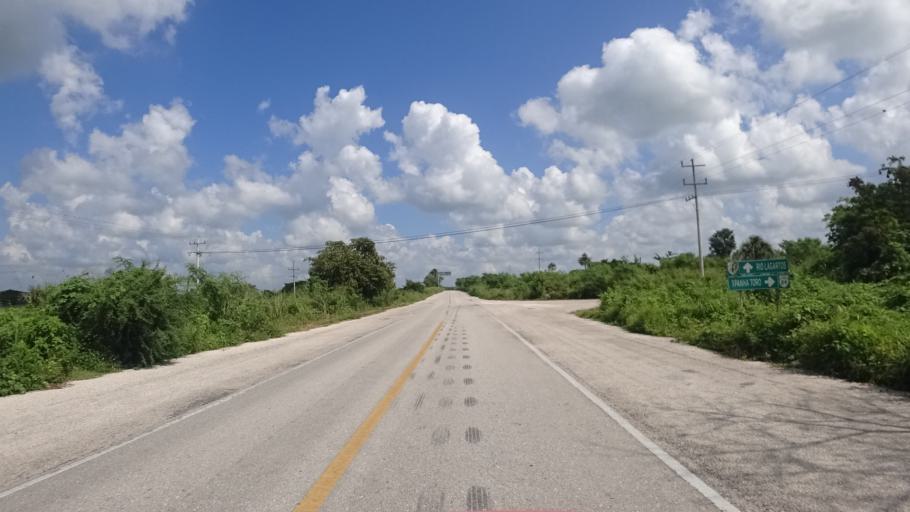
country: MX
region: Yucatan
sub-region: Panaba
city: Loche
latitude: 21.3224
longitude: -88.1636
